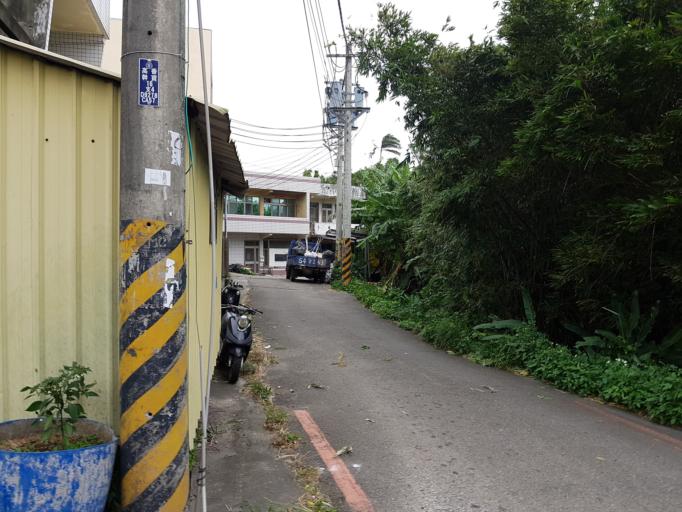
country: TW
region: Taiwan
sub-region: Hsinchu
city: Hsinchu
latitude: 24.7570
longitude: 120.9473
